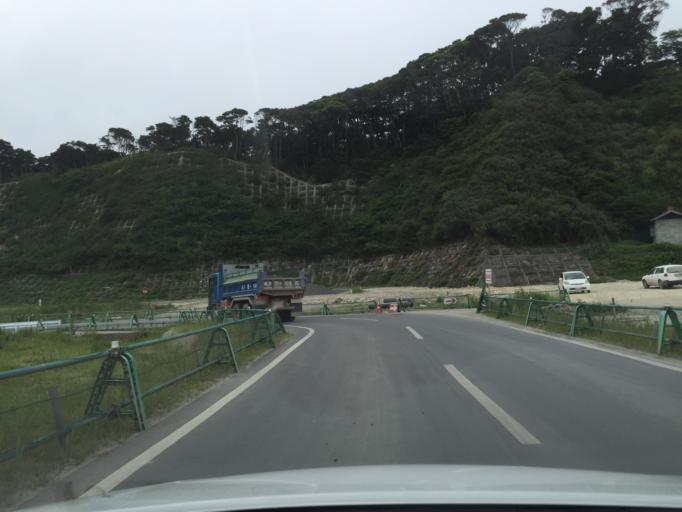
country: JP
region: Fukushima
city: Iwaki
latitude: 37.0066
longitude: 140.9776
